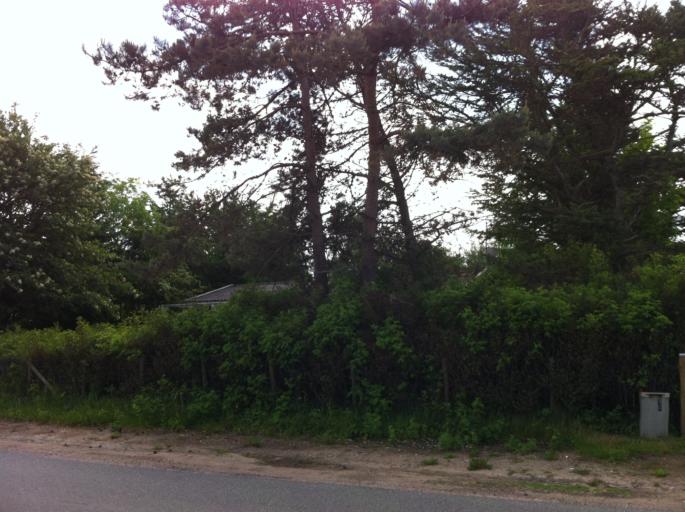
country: DK
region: Capital Region
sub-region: Gribskov Kommune
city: Gilleleje
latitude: 56.1233
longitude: 12.2607
